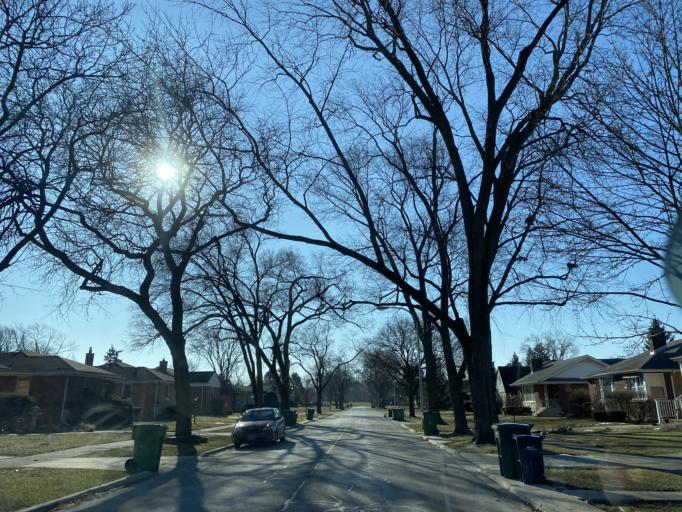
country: US
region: Illinois
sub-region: Cook County
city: Westchester
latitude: 41.8518
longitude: -87.8697
